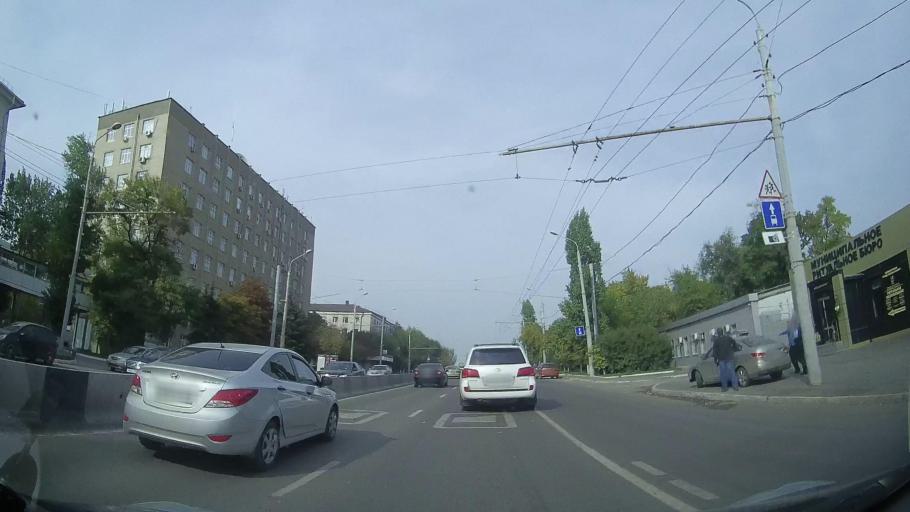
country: RU
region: Rostov
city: Rostov-na-Donu
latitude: 47.2380
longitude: 39.7136
